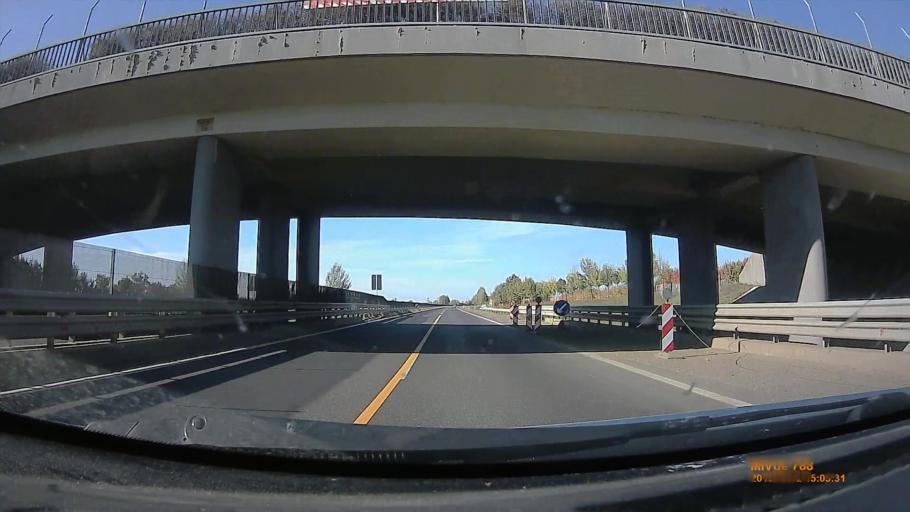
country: HU
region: Hajdu-Bihar
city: Hajduboszormeny
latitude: 47.5822
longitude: 21.5334
